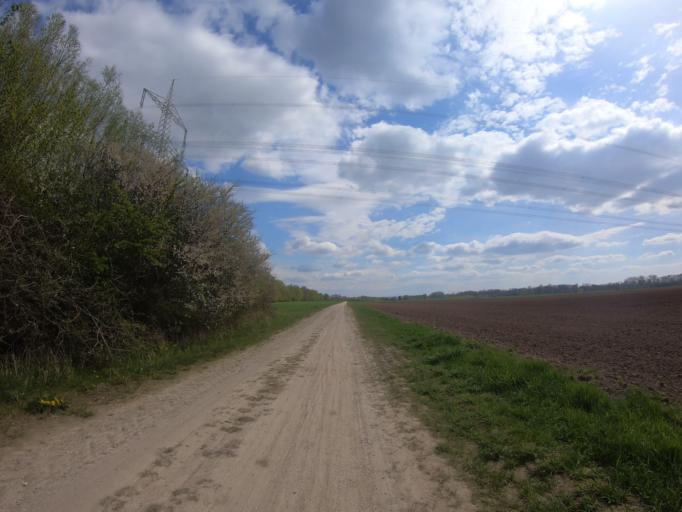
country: DE
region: Lower Saxony
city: Sarstedt
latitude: 52.2593
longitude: 9.8216
